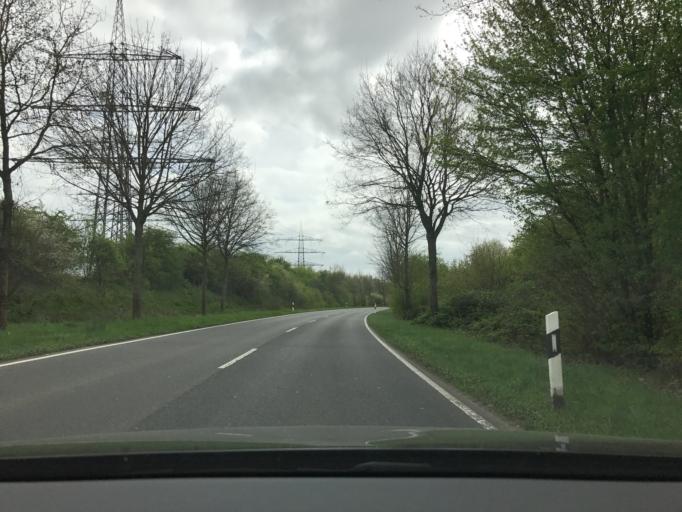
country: DE
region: North Rhine-Westphalia
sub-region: Regierungsbezirk Dusseldorf
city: Kaarst
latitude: 51.2621
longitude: 6.6103
